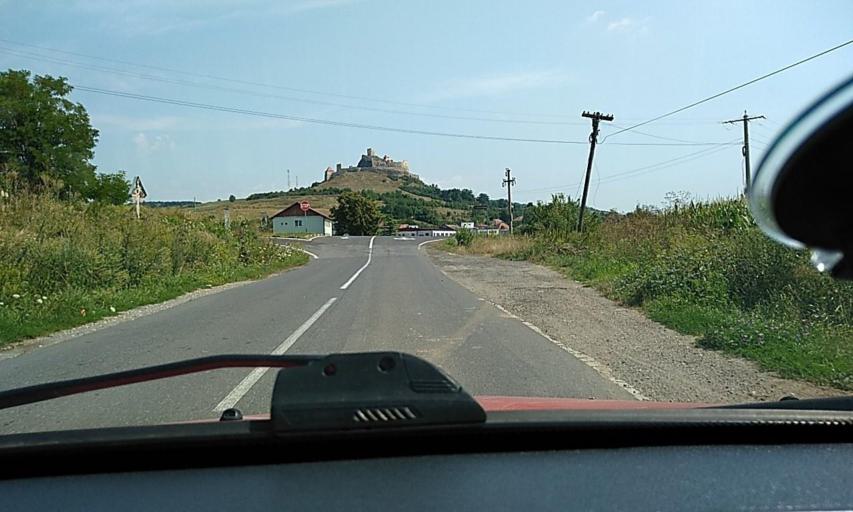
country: RO
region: Brasov
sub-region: Oras Rupea
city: Rupea
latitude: 46.0291
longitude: 25.2042
